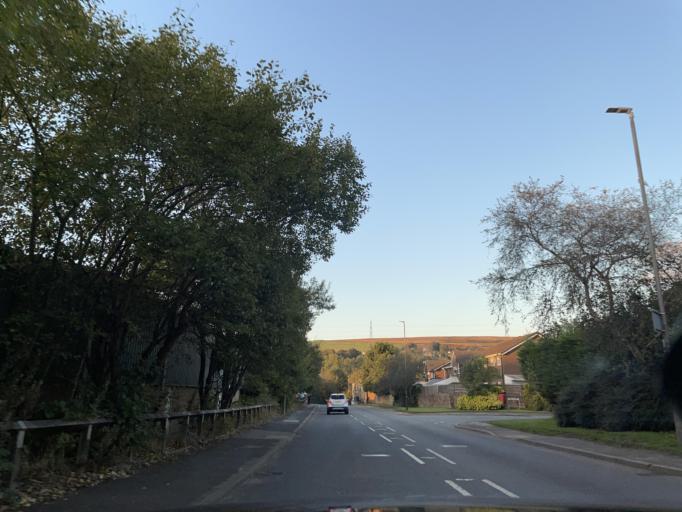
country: GB
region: England
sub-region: Borough of Tameside
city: Longdendale
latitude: 53.4665
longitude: -1.9710
